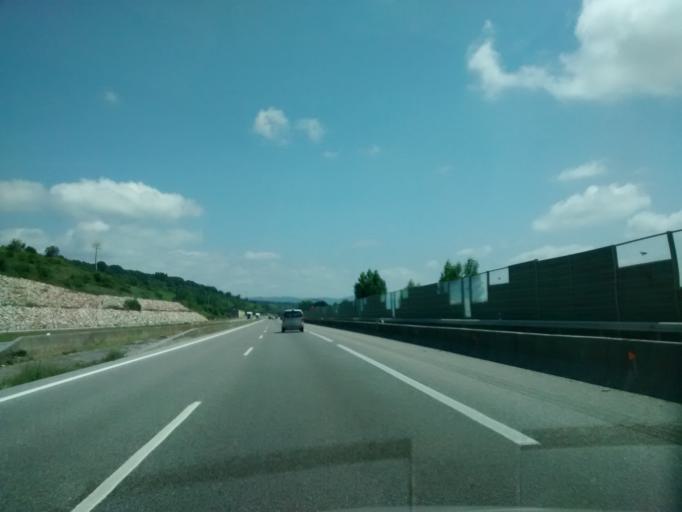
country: ES
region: Castille and Leon
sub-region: Provincia de Leon
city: Congosto
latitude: 42.5958
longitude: -6.5087
